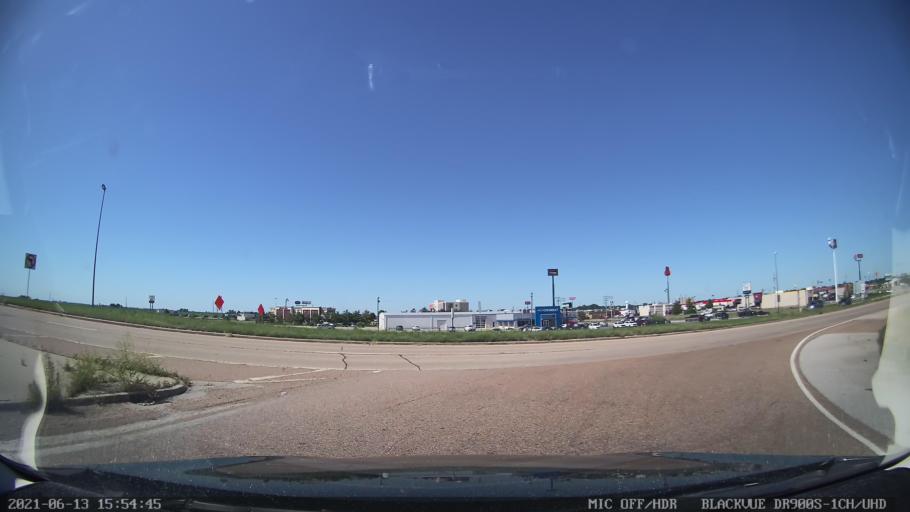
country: US
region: Illinois
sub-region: Montgomery County
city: Litchfield
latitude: 39.1752
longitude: -89.6780
